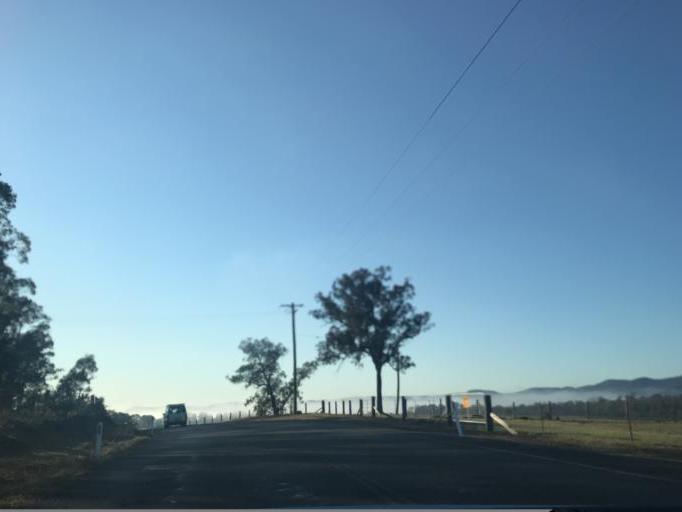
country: AU
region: New South Wales
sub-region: Cessnock
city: Cessnock
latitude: -32.9123
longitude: 151.2984
